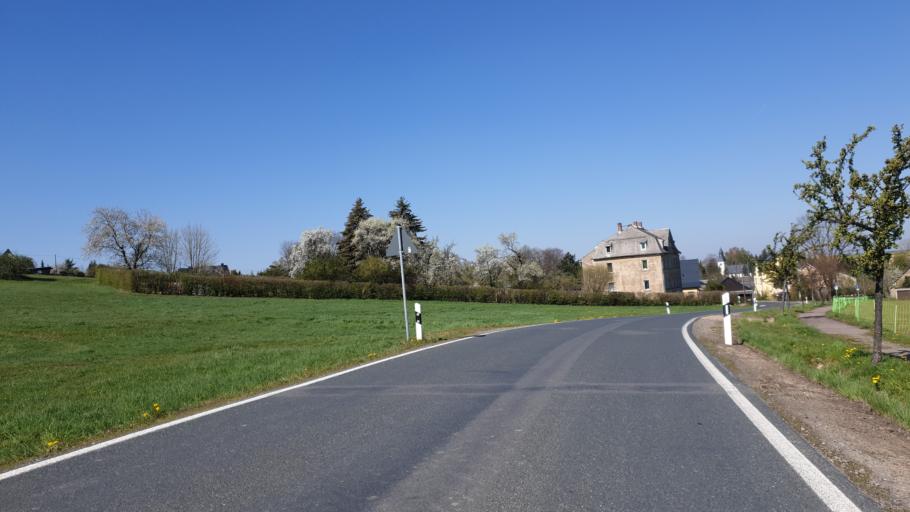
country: DE
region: Saxony
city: Taura
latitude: 50.9162
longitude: 12.8480
